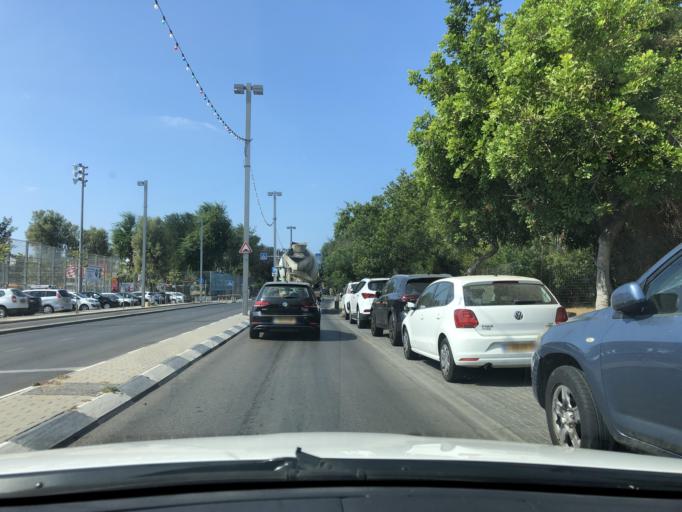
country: IL
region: Tel Aviv
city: Yafo
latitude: 32.0381
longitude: 34.7542
